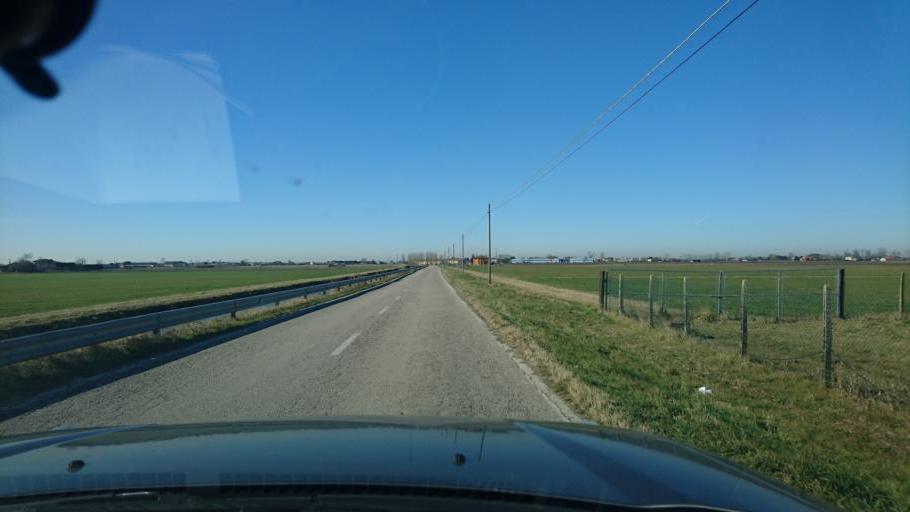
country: IT
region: Emilia-Romagna
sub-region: Provincia di Ferrara
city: Mesola
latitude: 44.9441
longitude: 12.2400
